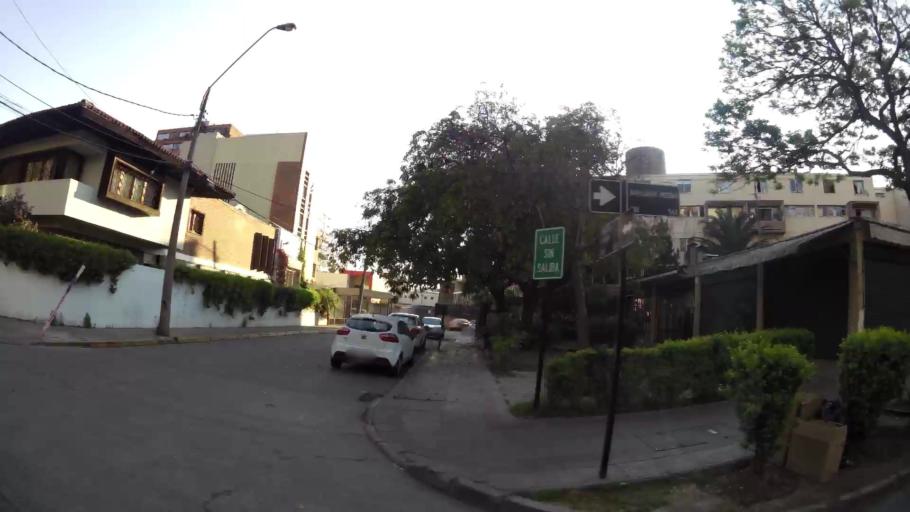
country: CL
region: Santiago Metropolitan
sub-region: Provincia de Santiago
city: Villa Presidente Frei, Nunoa, Santiago, Chile
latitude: -33.4298
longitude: -70.6124
